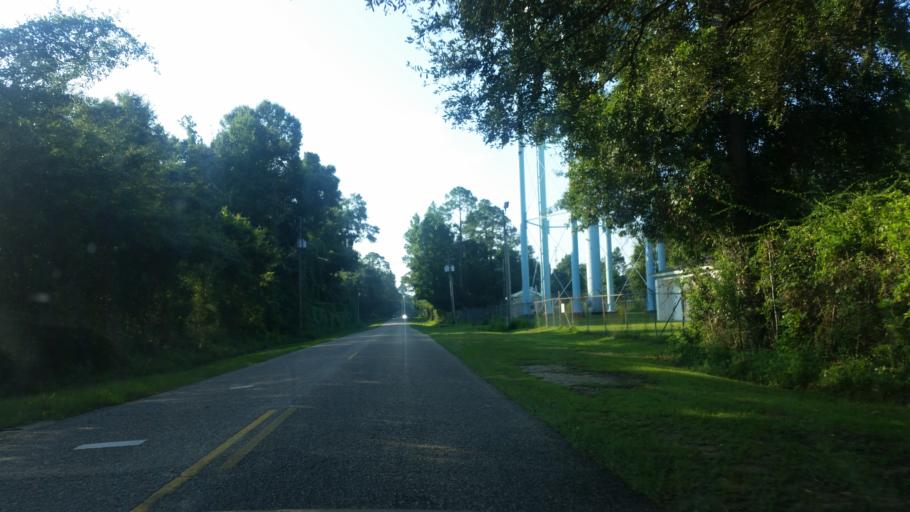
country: US
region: Florida
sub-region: Escambia County
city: Gonzalez
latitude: 30.5845
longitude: -87.2973
